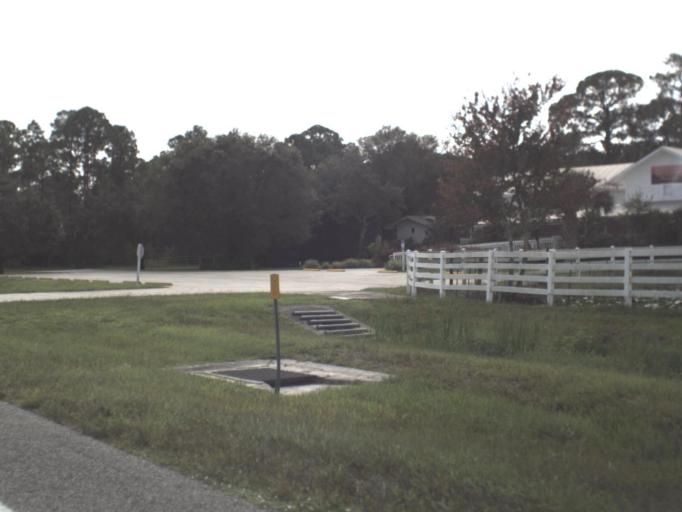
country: US
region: Florida
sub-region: Lee County
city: Alva
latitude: 26.7100
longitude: -81.6343
